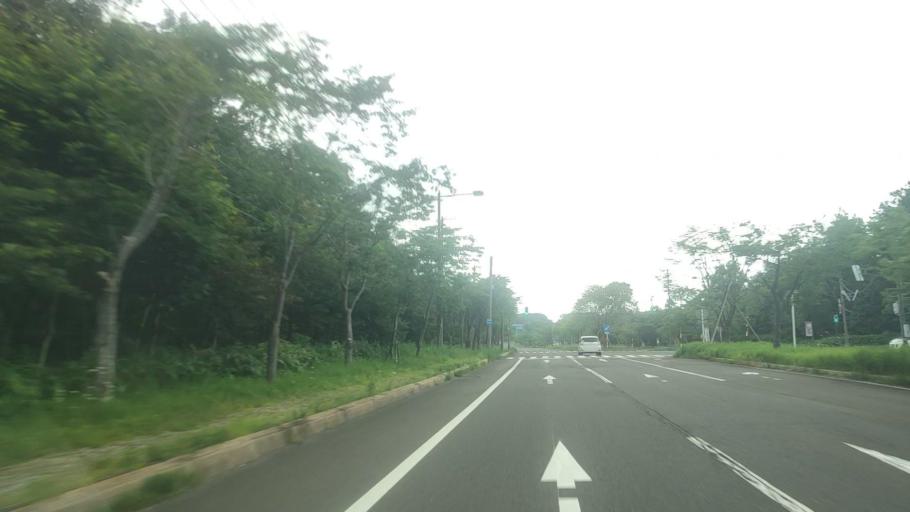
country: JP
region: Hokkaido
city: Shiraoi
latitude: 42.4672
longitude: 141.1655
